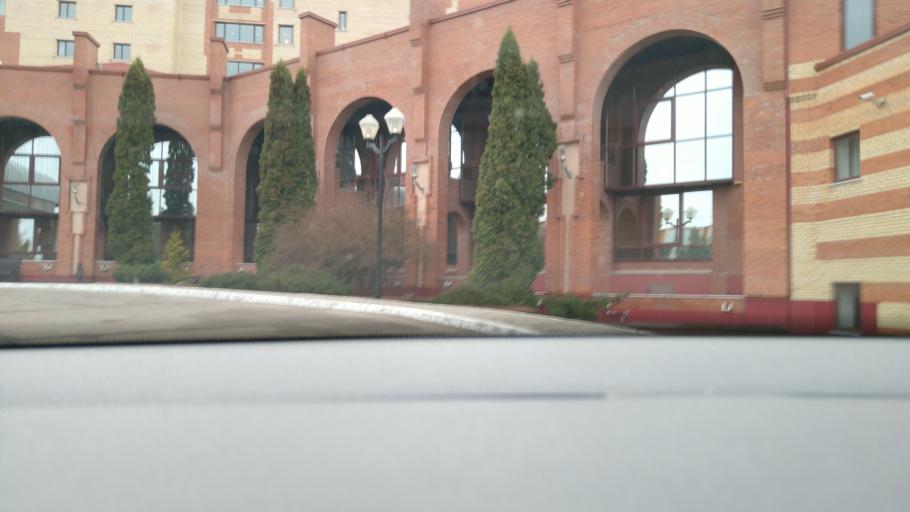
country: RU
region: Moskovskaya
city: Vatutinki
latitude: 55.5141
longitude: 37.3350
